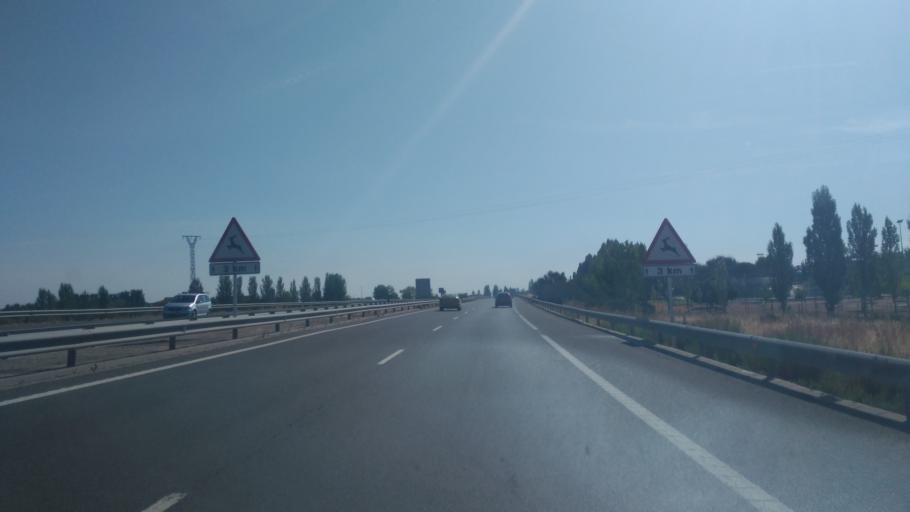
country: ES
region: Castille and Leon
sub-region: Provincia de Salamanca
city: Santa Marta de Tormes
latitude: 40.9446
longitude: -5.6309
